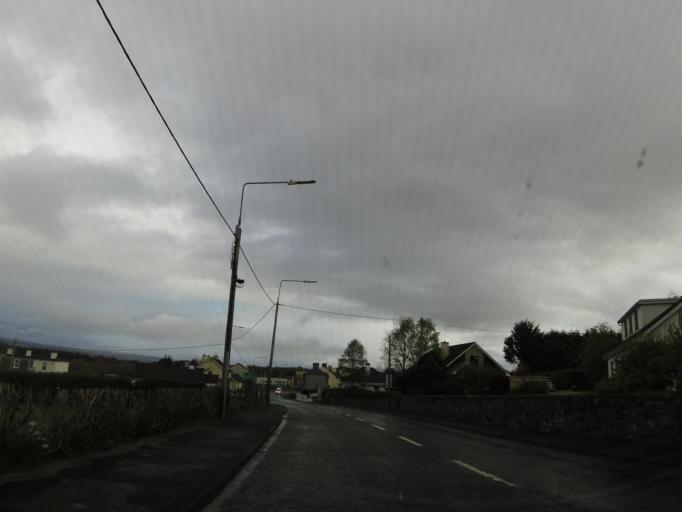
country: IE
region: Connaught
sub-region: Sligo
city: Tobercurry
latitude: 54.0502
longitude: -8.7348
